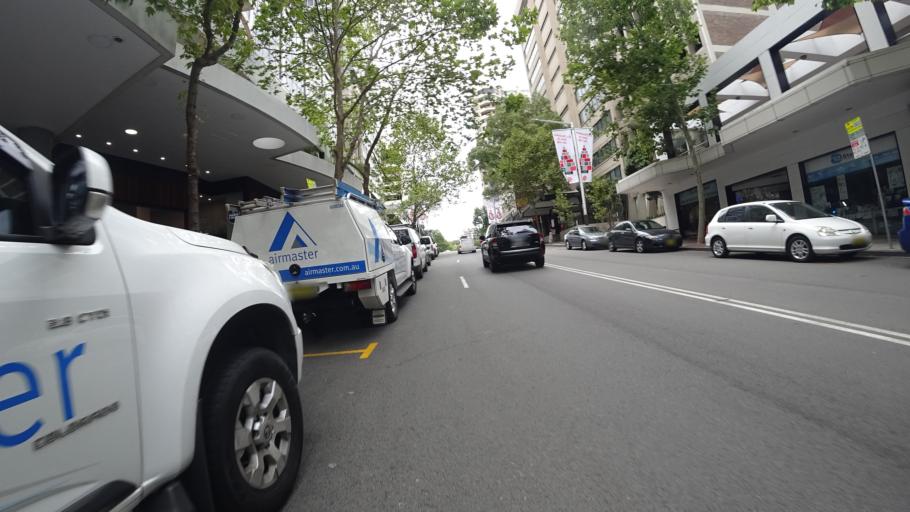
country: AU
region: New South Wales
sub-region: North Sydney
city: North Sydney
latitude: -33.8380
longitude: 151.2091
